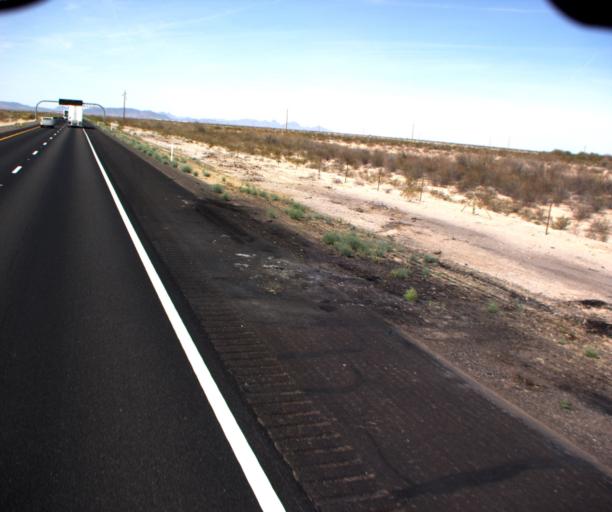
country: US
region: Arizona
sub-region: La Paz County
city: Salome
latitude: 33.6206
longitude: -113.6954
